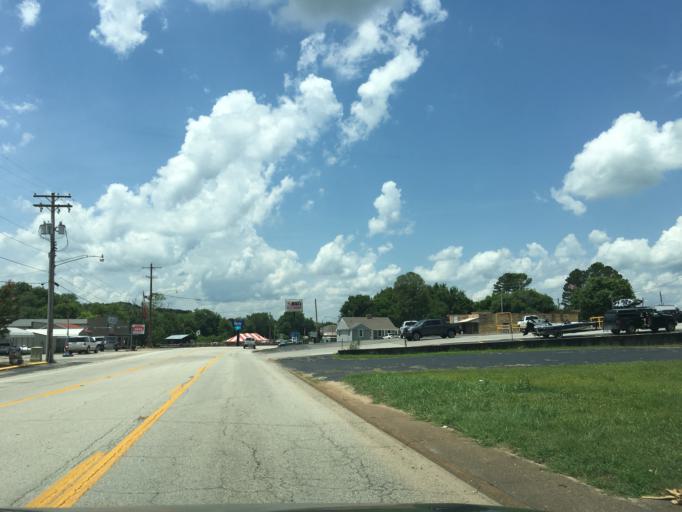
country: US
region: Arkansas
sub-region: Sharp County
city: Cherokee Village
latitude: 36.3156
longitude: -91.4842
